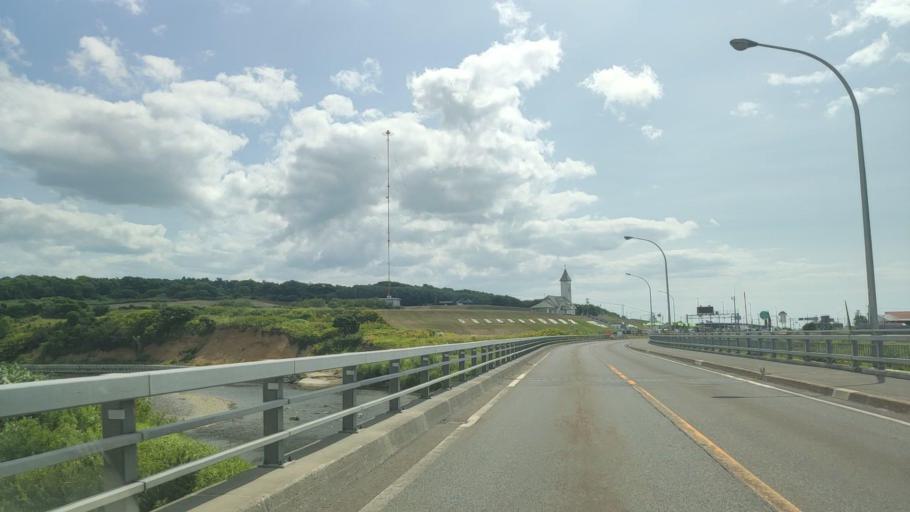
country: JP
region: Hokkaido
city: Makubetsu
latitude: 44.7174
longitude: 141.7932
